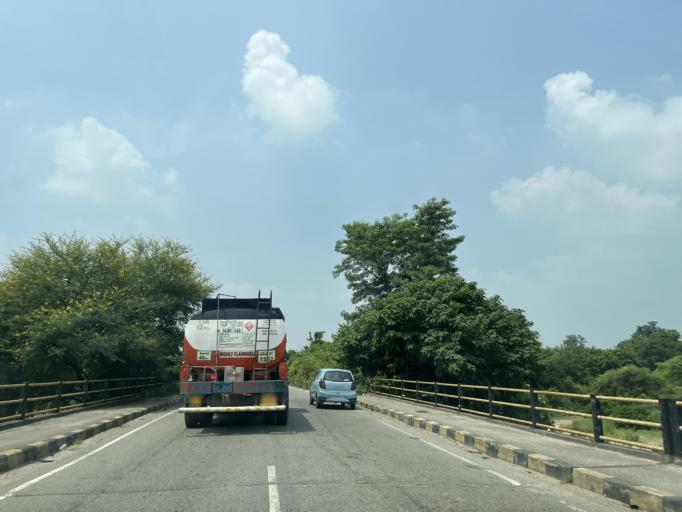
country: IN
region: Uttarakhand
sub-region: Haridwar
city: Haridwar
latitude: 29.8420
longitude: 78.1915
